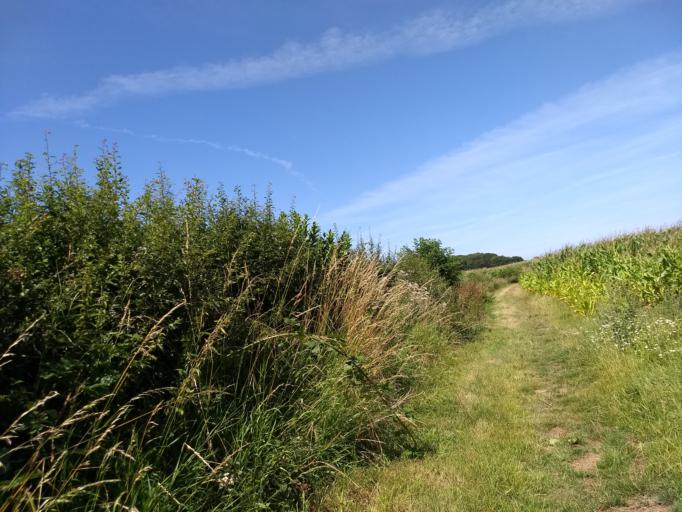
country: GB
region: England
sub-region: Isle of Wight
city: Brading
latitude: 50.6957
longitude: -1.1599
